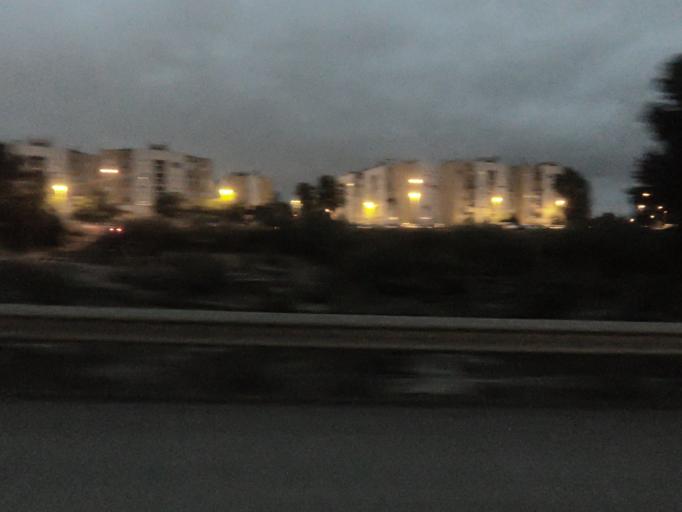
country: PT
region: Setubal
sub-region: Barreiro
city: Santo Antonio da Charneca
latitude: 38.6335
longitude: -9.0440
